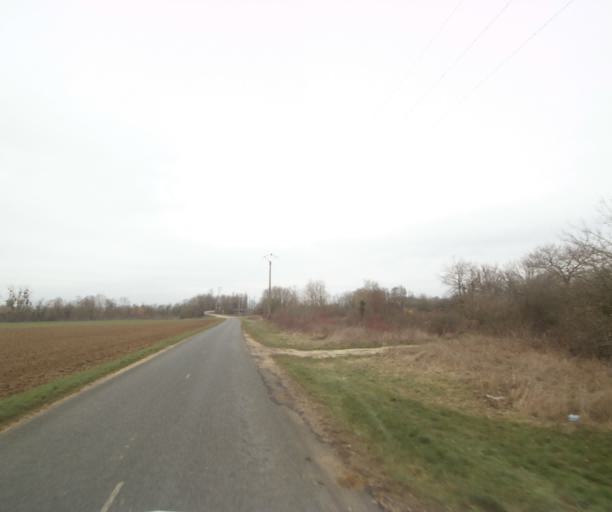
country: FR
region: Champagne-Ardenne
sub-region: Departement de la Haute-Marne
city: Villiers-en-Lieu
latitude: 48.6496
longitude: 4.8303
